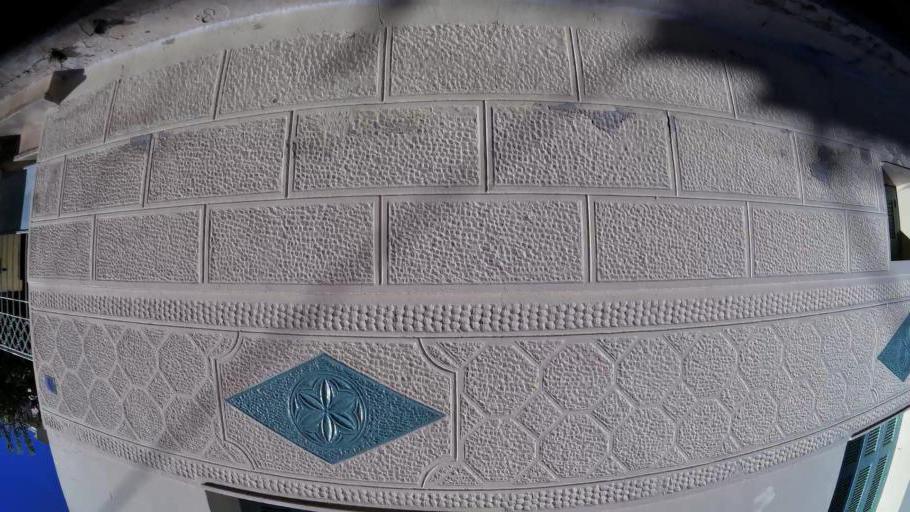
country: GR
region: Attica
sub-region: Nomarchia Anatolikis Attikis
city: Koropi
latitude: 37.9002
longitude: 23.8702
